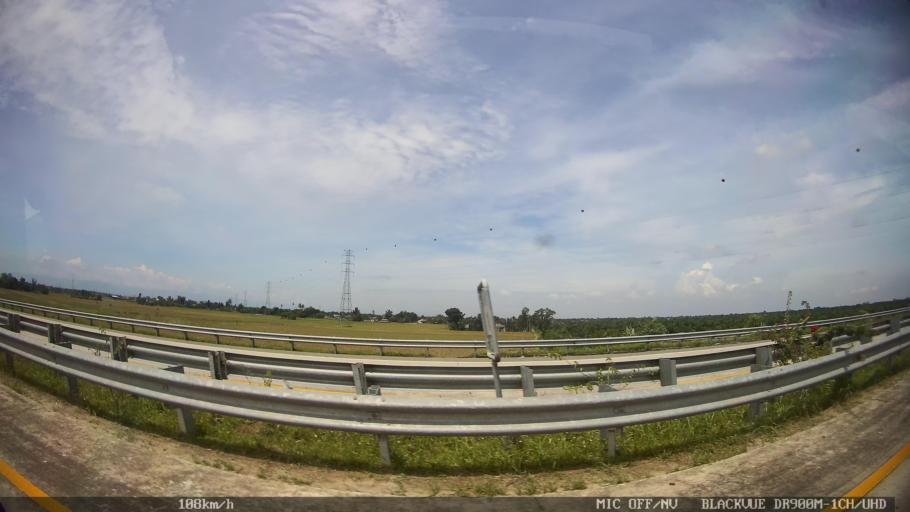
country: ID
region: North Sumatra
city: Percut
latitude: 3.5785
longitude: 98.8464
